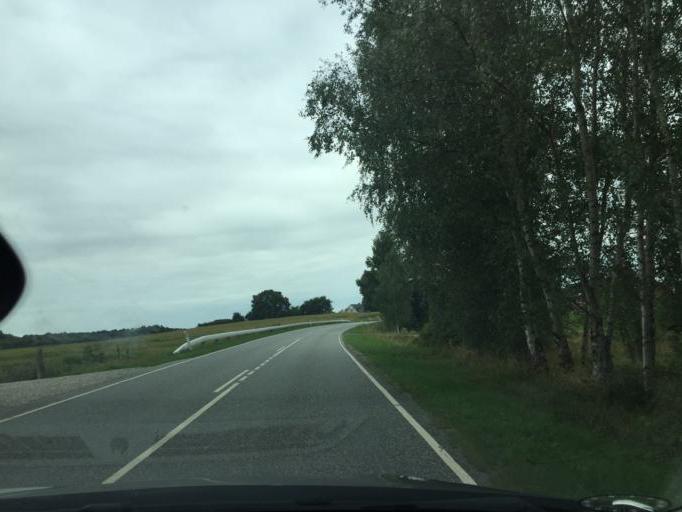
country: DK
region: South Denmark
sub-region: Assens Kommune
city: Arup
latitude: 55.3658
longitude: 10.0905
